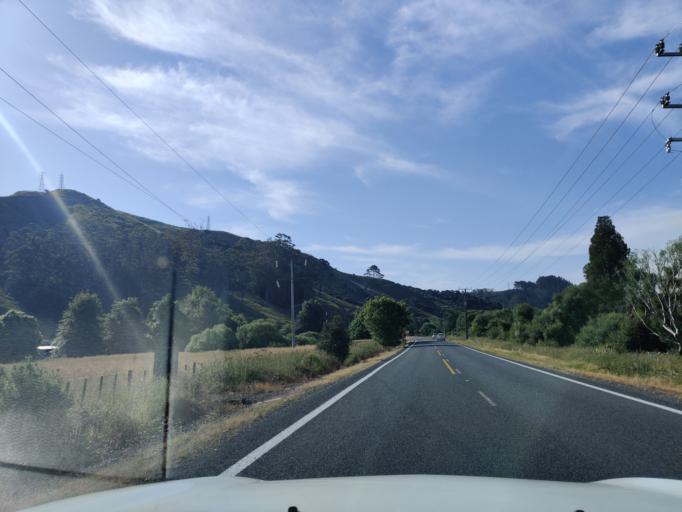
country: NZ
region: Waikato
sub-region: Waikato District
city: Ngaruawahia
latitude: -37.5999
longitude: 175.1594
